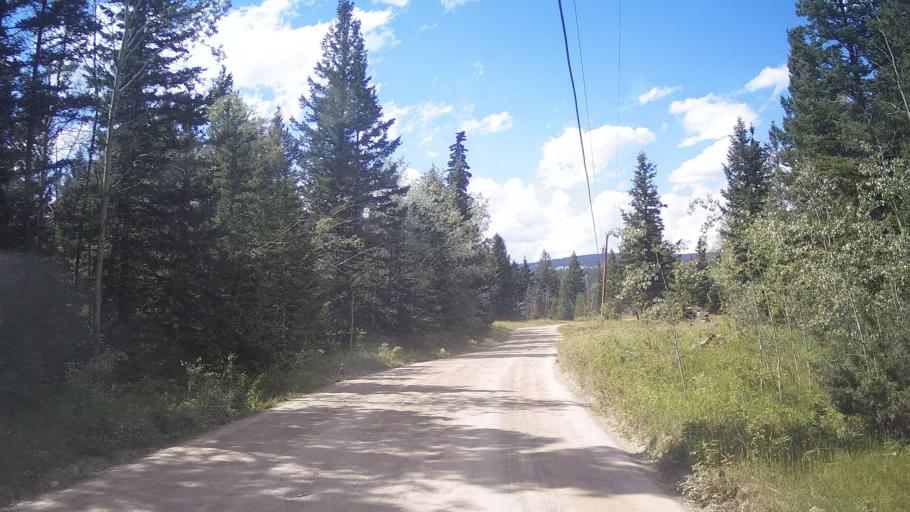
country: CA
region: British Columbia
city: Lillooet
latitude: 51.2656
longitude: -121.9737
